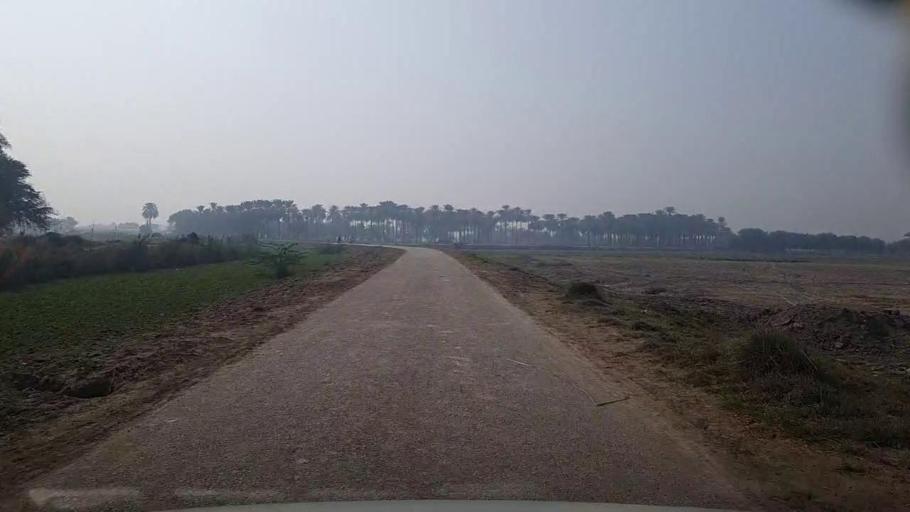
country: PK
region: Sindh
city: Setharja Old
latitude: 27.1931
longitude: 68.4773
